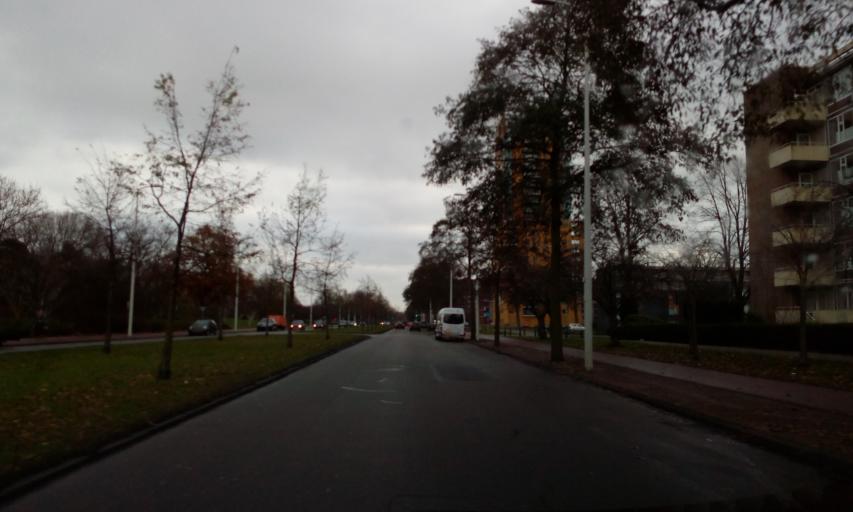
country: NL
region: South Holland
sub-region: Gemeente Den Haag
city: The Hague
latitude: 52.0511
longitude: 4.2807
